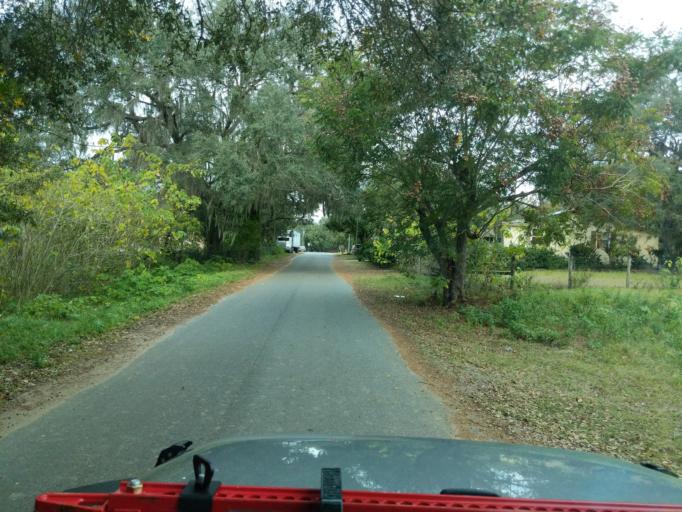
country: US
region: Florida
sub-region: Lake County
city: Mascotte
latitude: 28.5753
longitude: -81.9206
